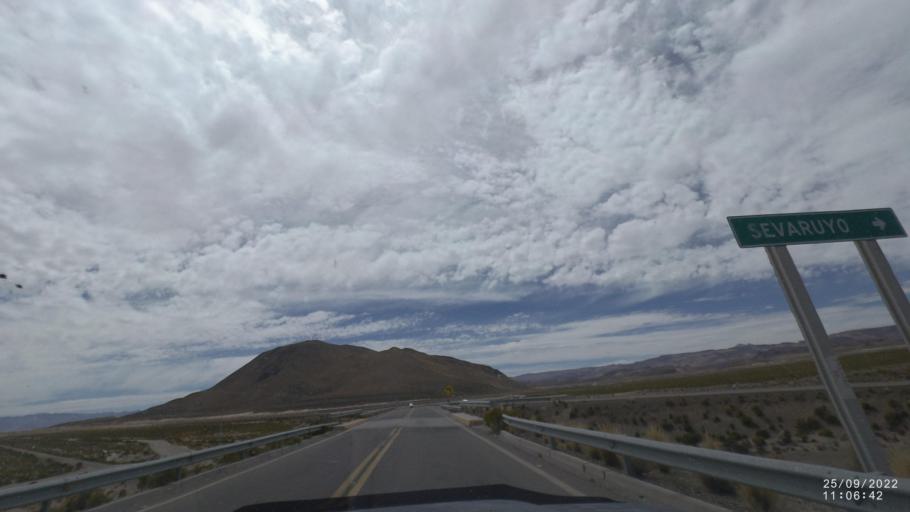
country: BO
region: Oruro
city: Challapata
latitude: -19.3544
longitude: -66.8593
